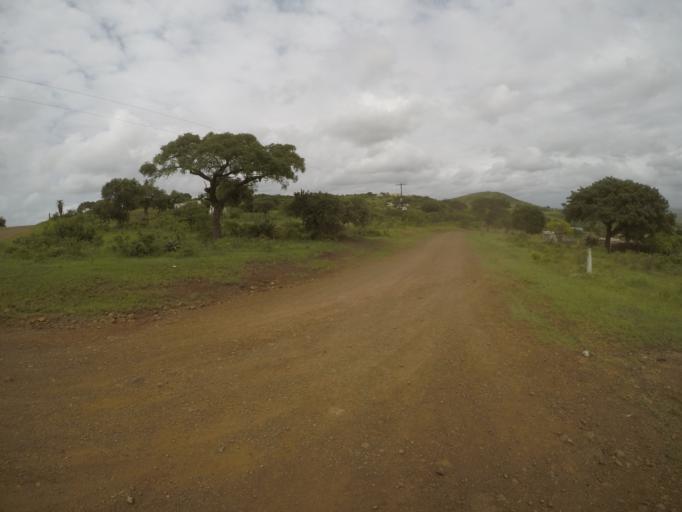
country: ZA
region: KwaZulu-Natal
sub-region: uThungulu District Municipality
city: Empangeni
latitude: -28.6131
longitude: 31.8986
